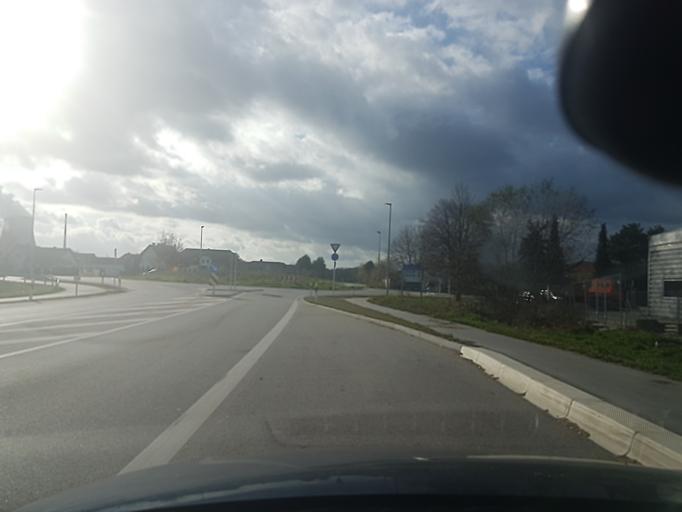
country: DE
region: Bavaria
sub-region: Lower Bavaria
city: Niederaichbach
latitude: 48.6181
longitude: 12.3085
